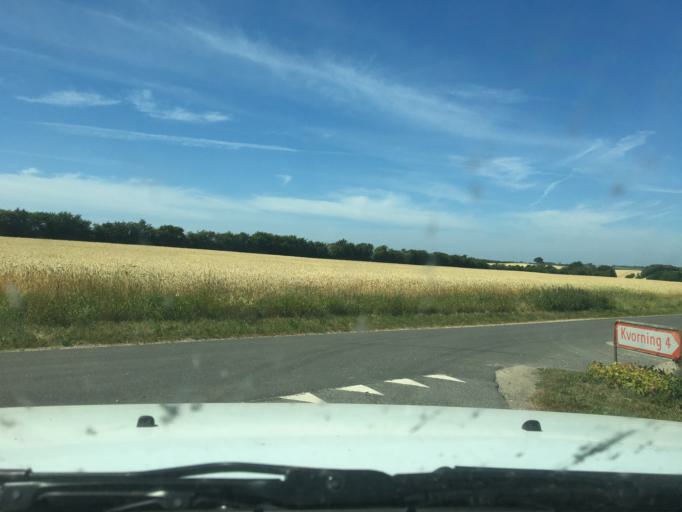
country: DK
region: Central Jutland
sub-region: Viborg Kommune
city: Bjerringbro
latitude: 56.5235
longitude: 9.6763
